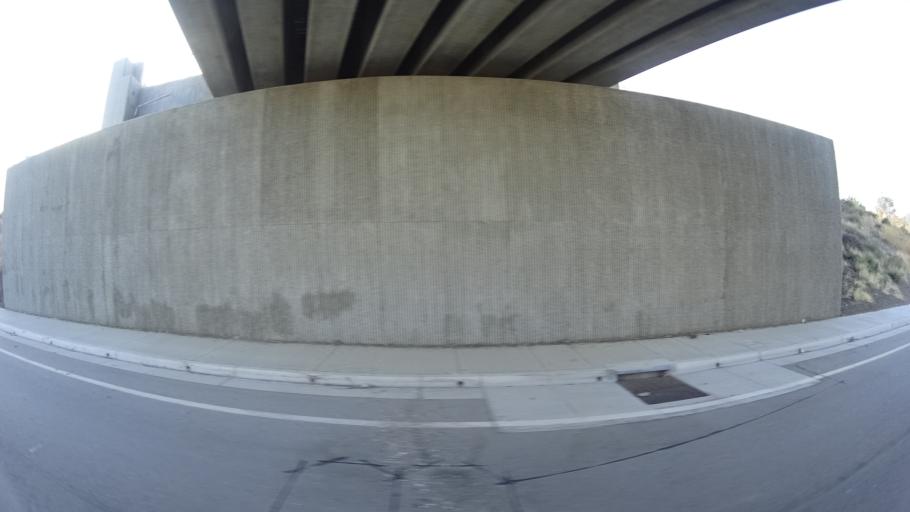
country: US
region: California
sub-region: Kern County
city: Rosedale
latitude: 35.3989
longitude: -119.1467
